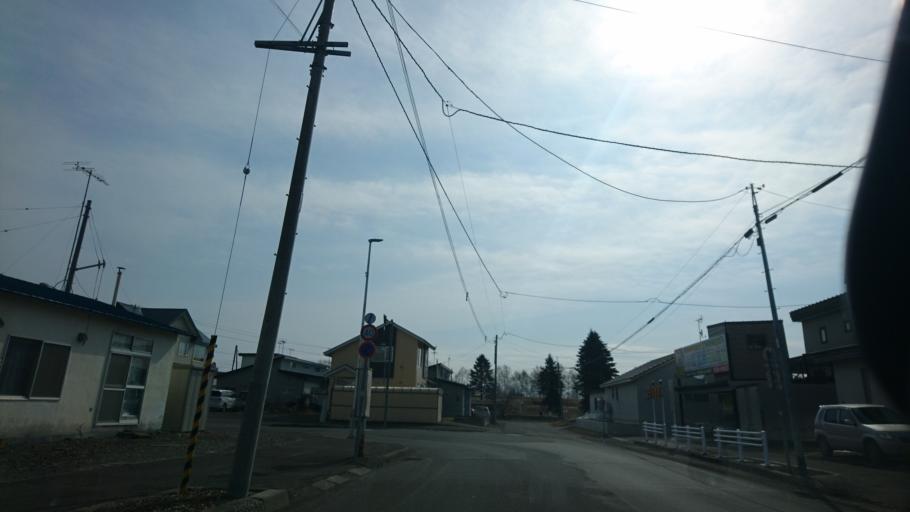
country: JP
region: Hokkaido
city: Obihiro
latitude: 42.9401
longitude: 143.2056
